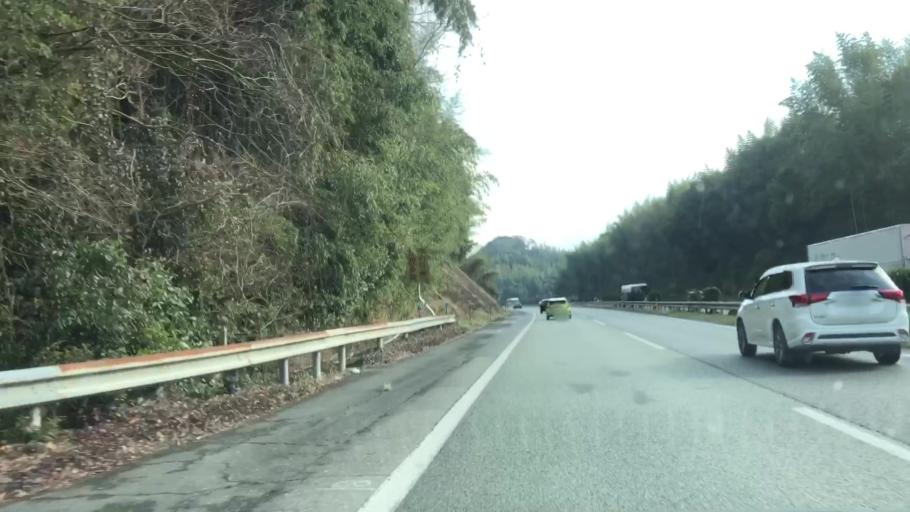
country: JP
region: Kumamoto
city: Tamana
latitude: 32.9996
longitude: 130.5912
